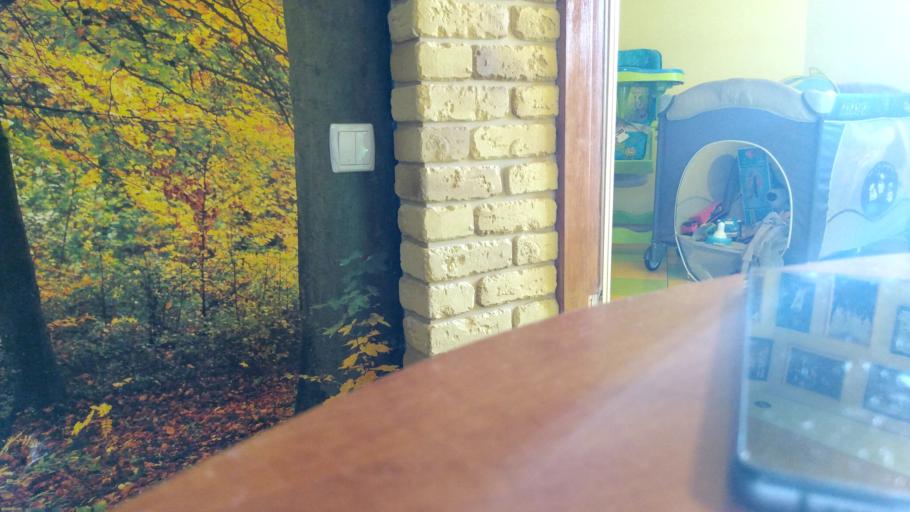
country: RU
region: Tverskaya
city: Likhoslavl'
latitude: 57.1272
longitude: 35.6499
